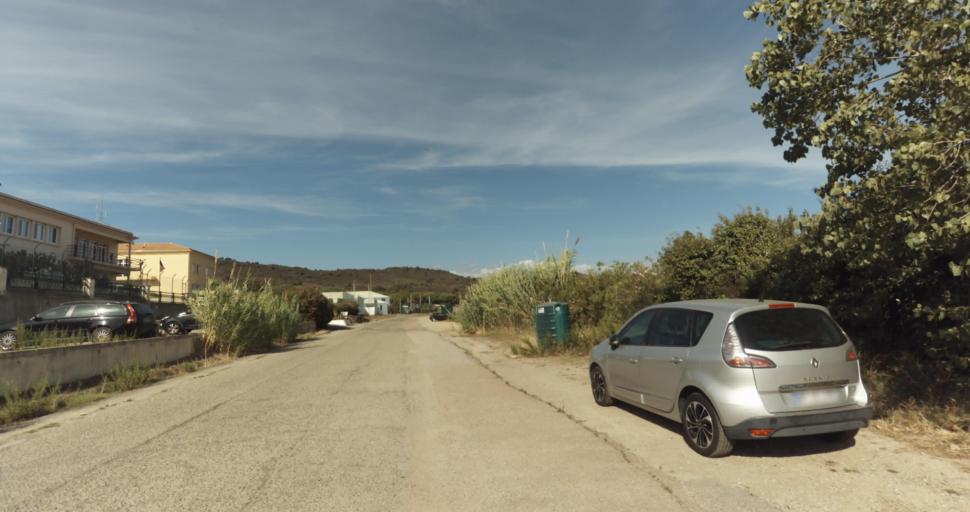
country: FR
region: Corsica
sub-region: Departement de la Corse-du-Sud
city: Ajaccio
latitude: 41.9264
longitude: 8.7667
